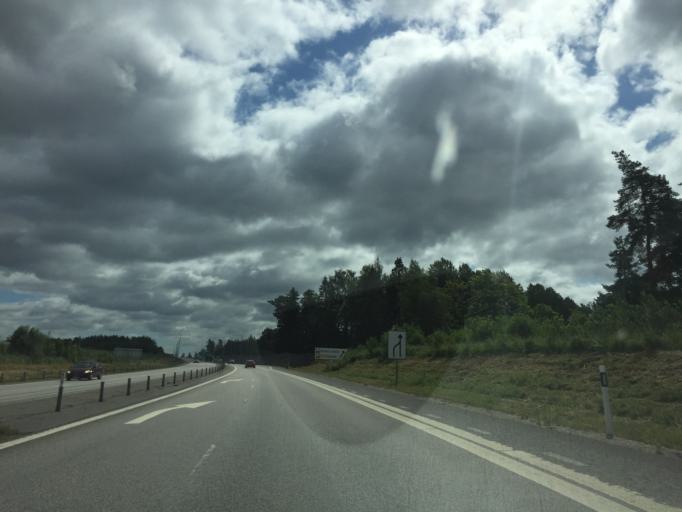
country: SE
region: OErebro
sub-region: Orebro Kommun
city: Orebro
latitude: 59.2396
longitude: 15.1104
